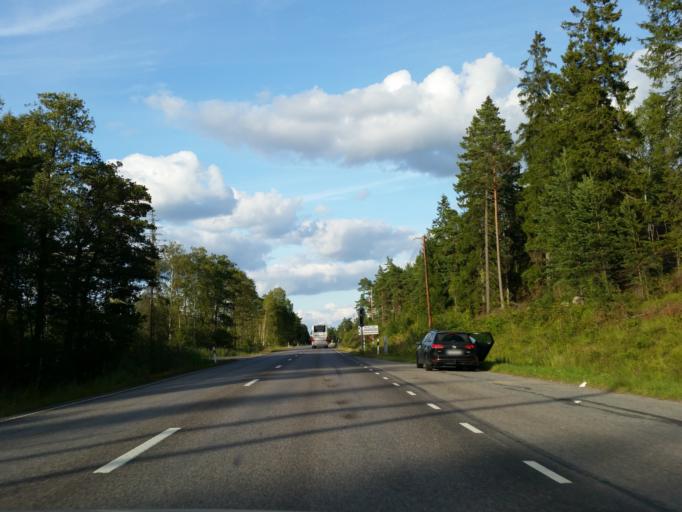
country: SE
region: Stockholm
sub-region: Sodertalje Kommun
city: Molnbo
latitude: 59.0670
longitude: 17.5265
